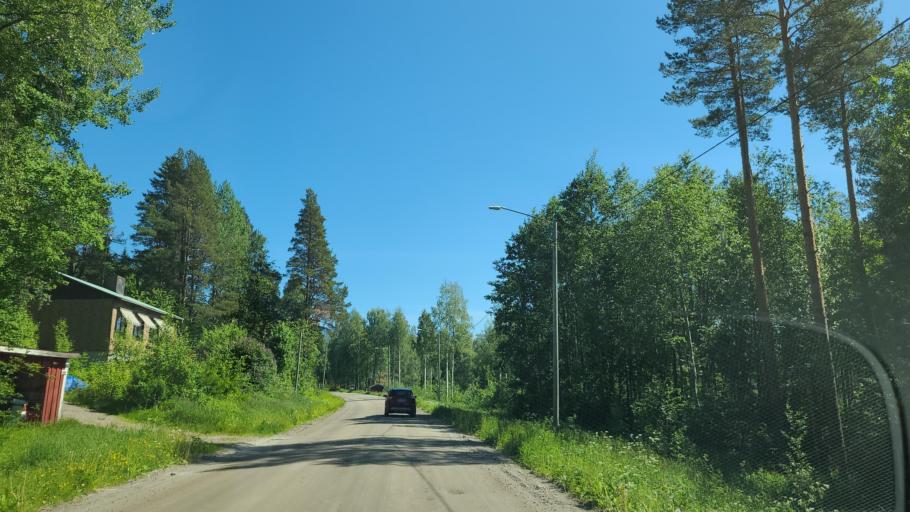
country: SE
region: Vaesterbotten
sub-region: Bjurholms Kommun
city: Bjurholm
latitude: 63.6863
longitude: 18.9629
